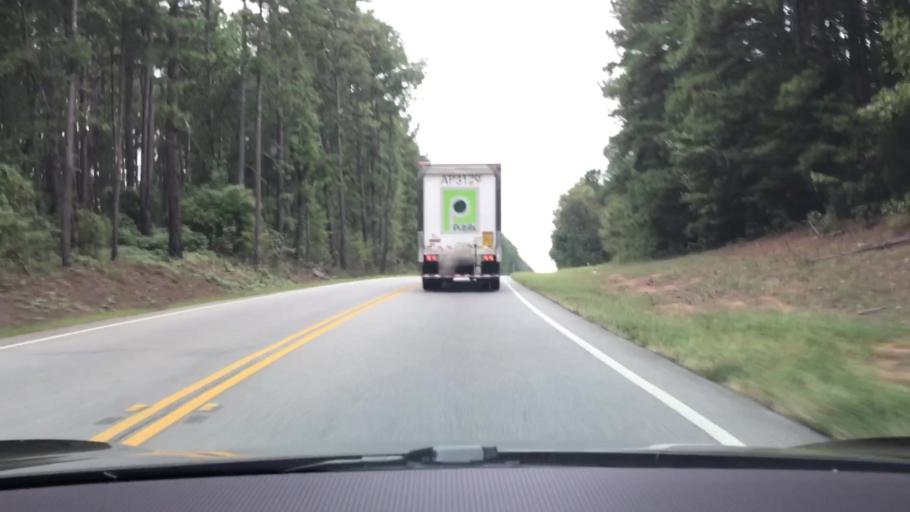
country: US
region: Georgia
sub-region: Greene County
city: Greensboro
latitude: 33.6808
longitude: -83.2716
